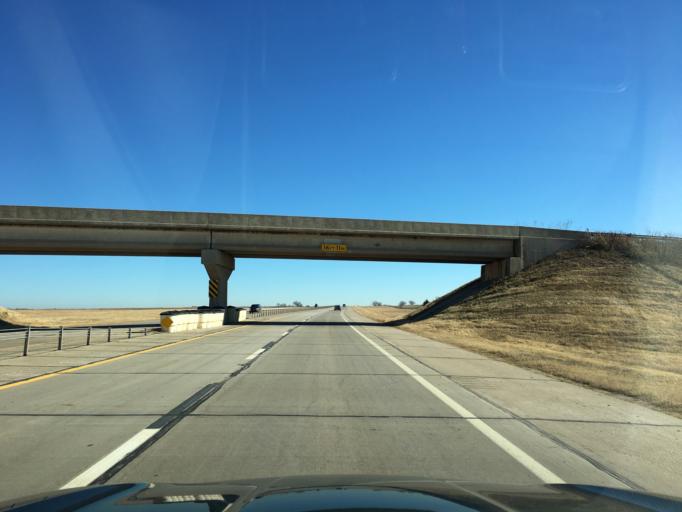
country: US
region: Oklahoma
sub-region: Noble County
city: Perry
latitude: 36.4015
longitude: -97.2477
